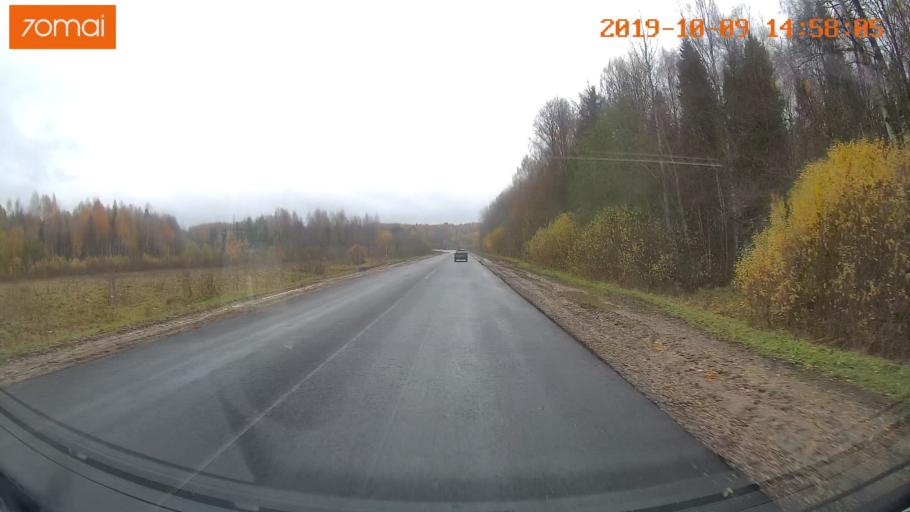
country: RU
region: Kostroma
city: Chistyye Bory
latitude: 58.3306
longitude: 41.6534
